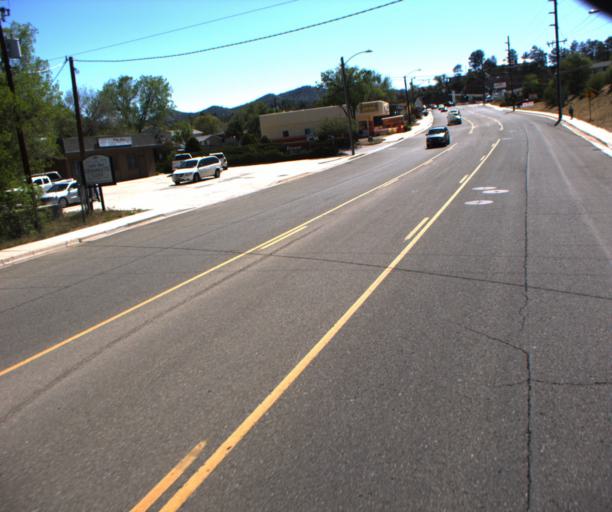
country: US
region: Arizona
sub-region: Yavapai County
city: Prescott
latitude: 34.5306
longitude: -112.4736
